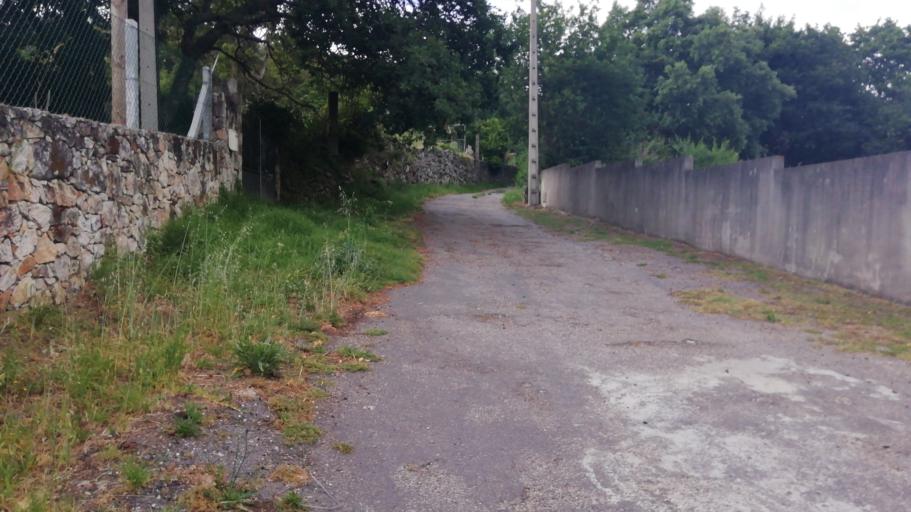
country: ES
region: Galicia
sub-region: Provincia de Pontevedra
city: A Guarda
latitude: 41.8840
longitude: -8.8606
